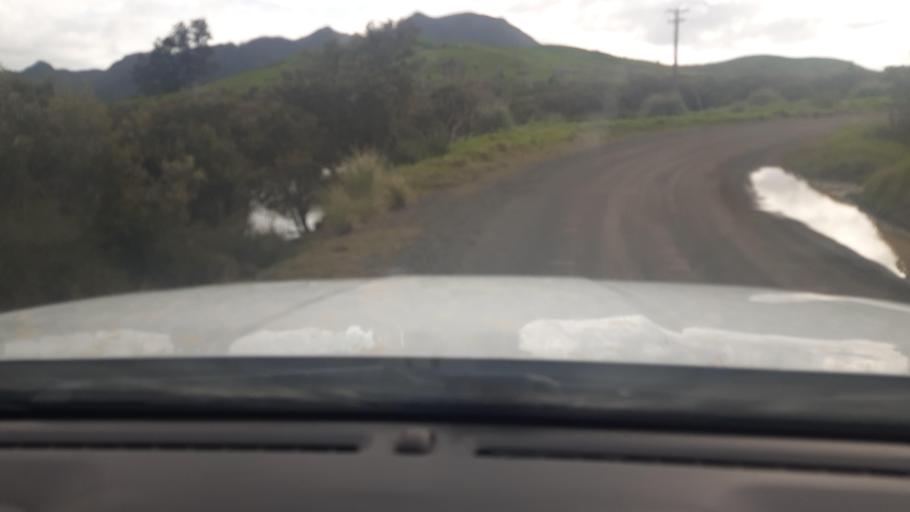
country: NZ
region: Northland
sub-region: Far North District
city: Ahipara
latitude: -35.2566
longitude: 173.2045
